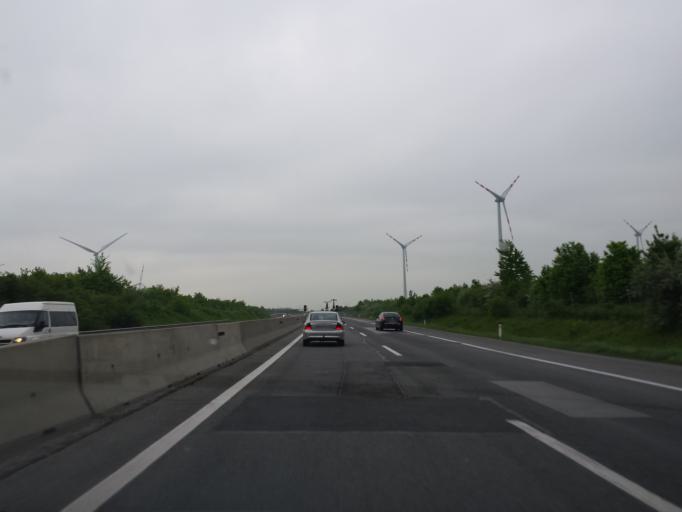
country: AT
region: Burgenland
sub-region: Politischer Bezirk Neusiedl am See
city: Zurndorf
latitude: 47.9386
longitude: 16.9774
